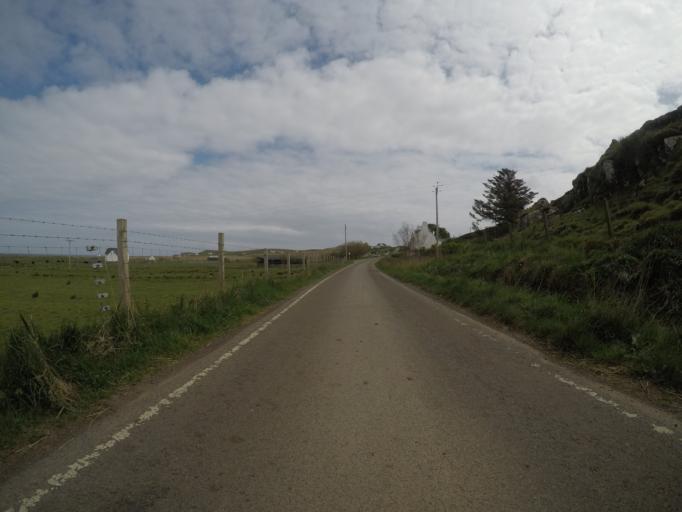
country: GB
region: Scotland
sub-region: Highland
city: Portree
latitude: 57.6847
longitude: -6.3078
